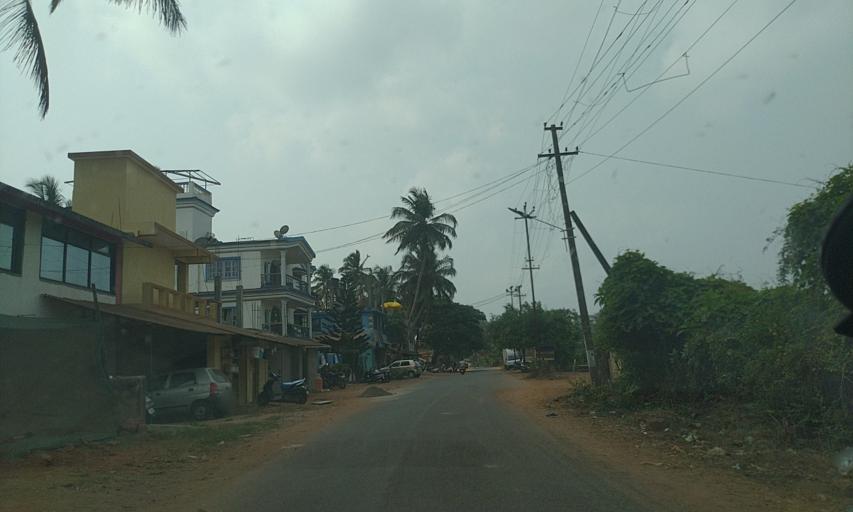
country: IN
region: Goa
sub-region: North Goa
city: Taleigao
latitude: 15.4691
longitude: 73.8280
